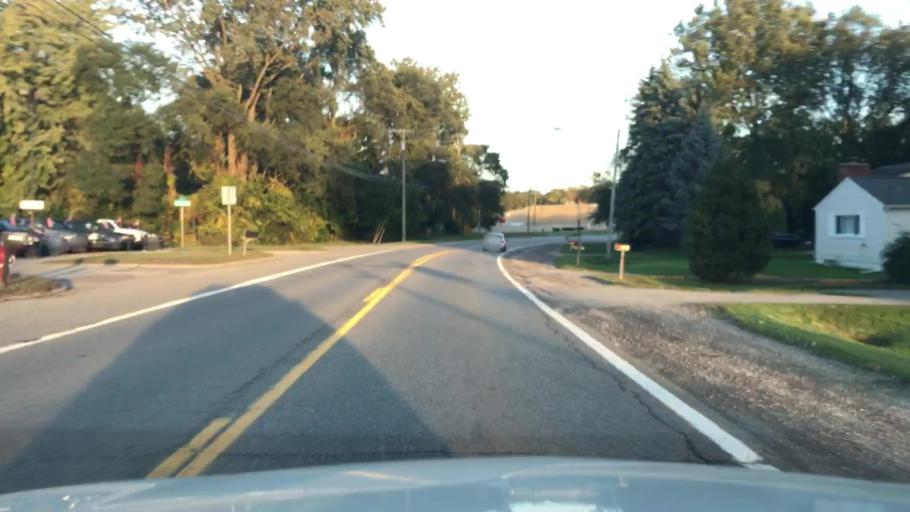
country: US
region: Michigan
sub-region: Macomb County
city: Utica
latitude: 42.6394
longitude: -83.0630
